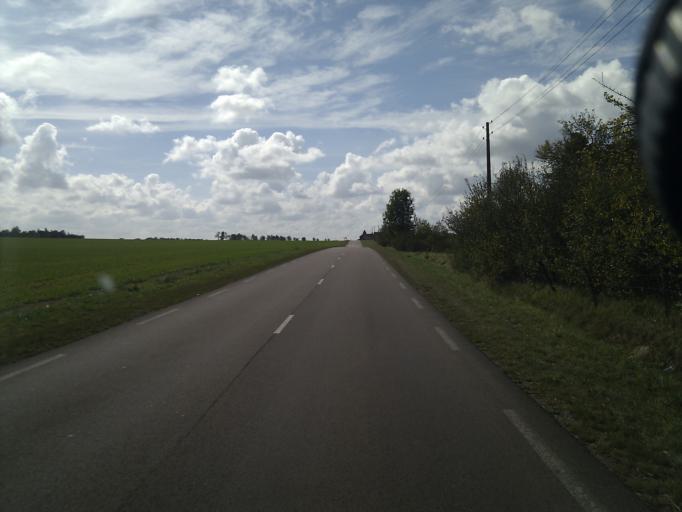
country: FR
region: Bourgogne
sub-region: Departement de la Cote-d'Or
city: Chatillon-sur-Seine
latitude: 47.8368
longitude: 4.5479
